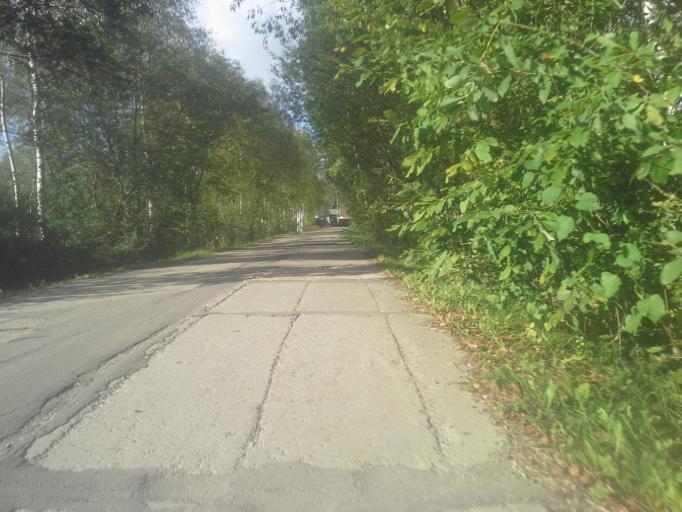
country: RU
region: Moskovskaya
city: Kievskij
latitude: 55.3552
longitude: 36.9014
